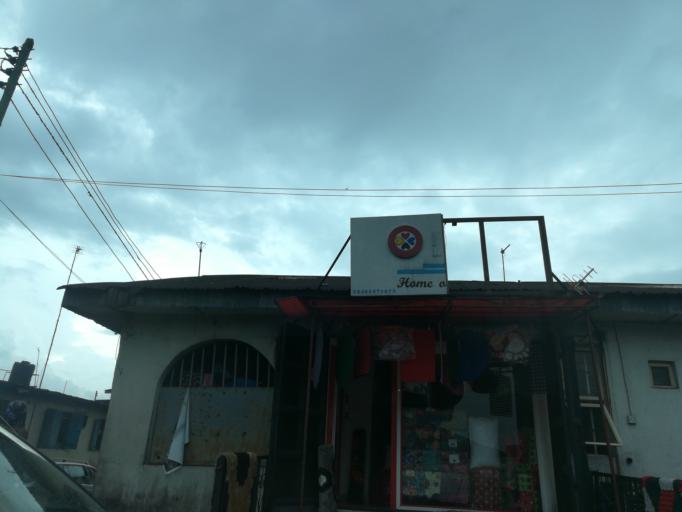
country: NG
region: Rivers
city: Port Harcourt
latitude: 4.8151
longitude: 7.0121
